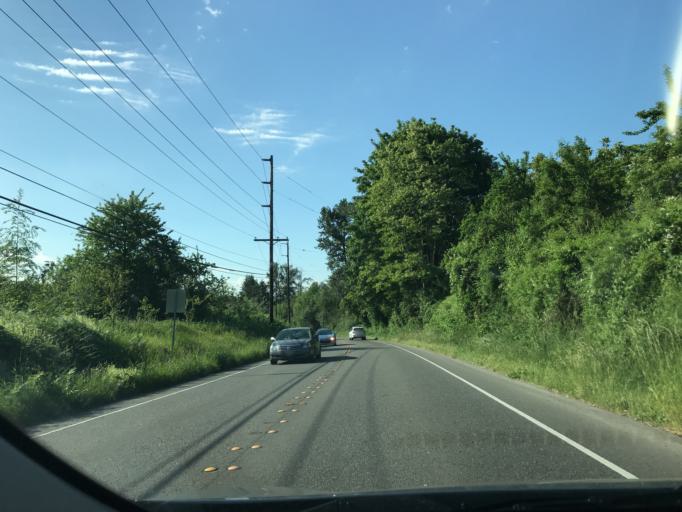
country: US
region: Washington
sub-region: King County
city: Issaquah
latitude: 47.5126
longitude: -122.0234
